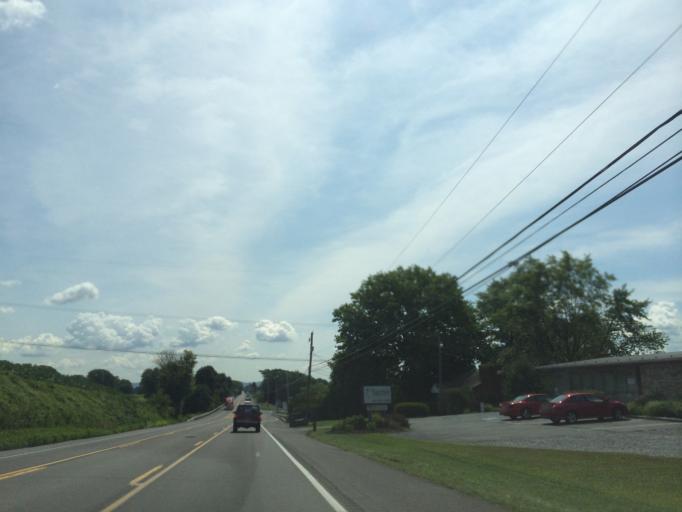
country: US
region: Pennsylvania
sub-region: Lehigh County
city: Breinigsville
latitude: 40.5417
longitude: -75.6481
